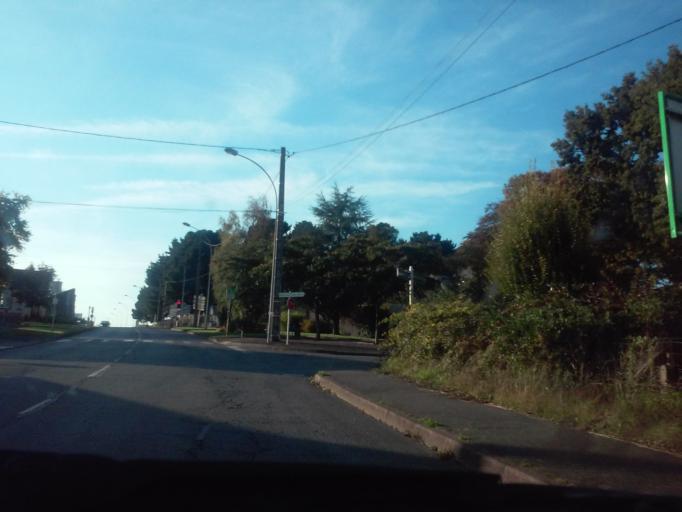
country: FR
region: Pays de la Loire
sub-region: Departement de la Loire-Atlantique
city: Pontchateau
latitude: 47.4402
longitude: -2.0931
